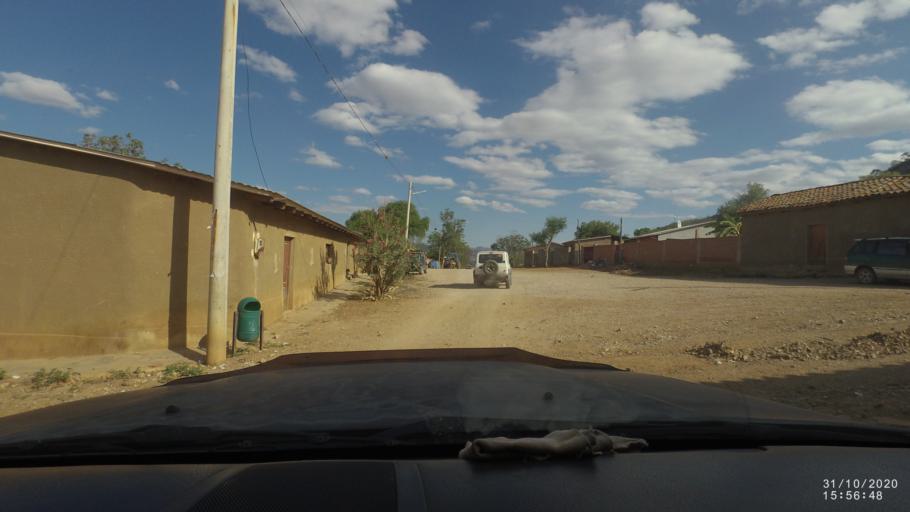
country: BO
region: Chuquisaca
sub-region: Provincia Zudanez
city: Mojocoya
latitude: -18.3230
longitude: -64.6757
